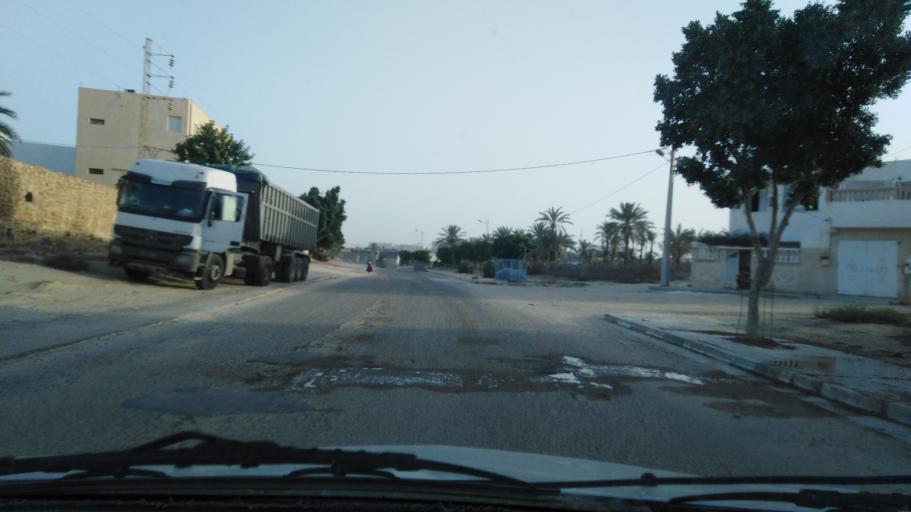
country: TN
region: Qabis
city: Gabes
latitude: 33.9584
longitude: 9.9957
